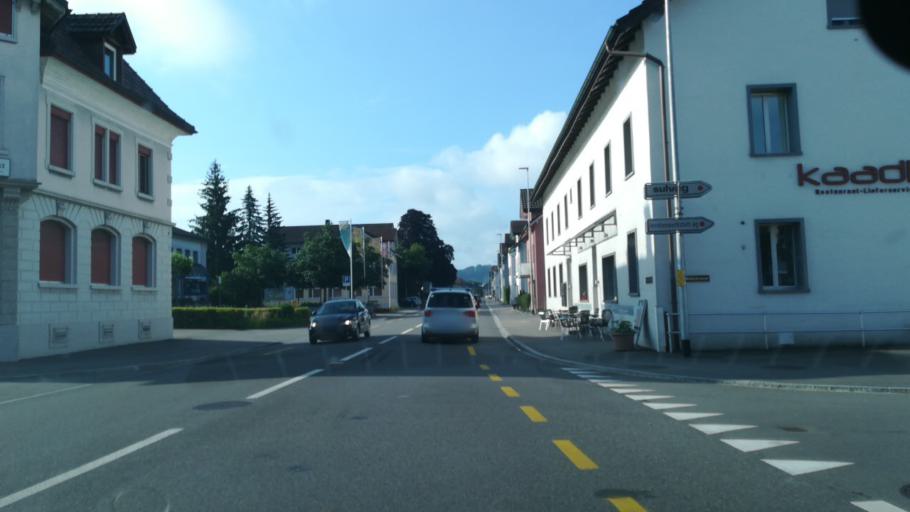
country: CH
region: Thurgau
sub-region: Weinfelden District
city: Sulgen
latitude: 47.5371
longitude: 9.1860
